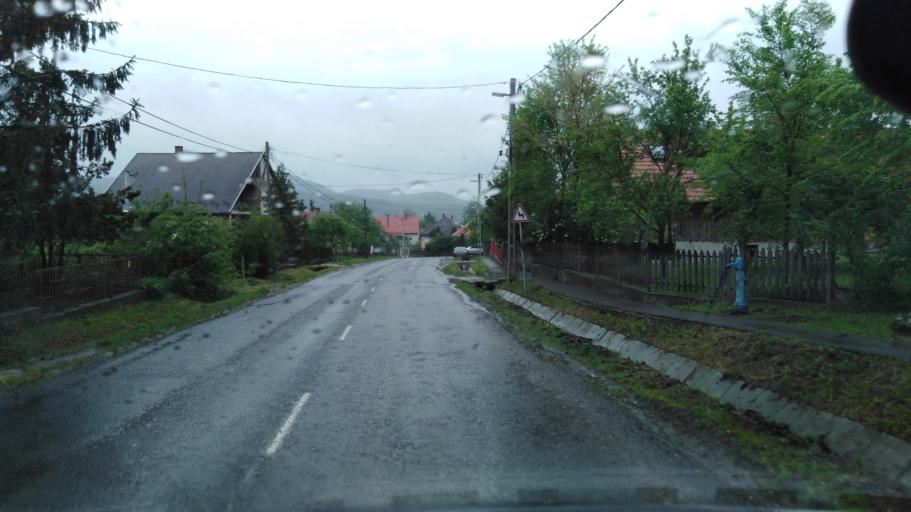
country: HU
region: Nograd
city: Bujak
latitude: 47.9493
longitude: 19.5984
